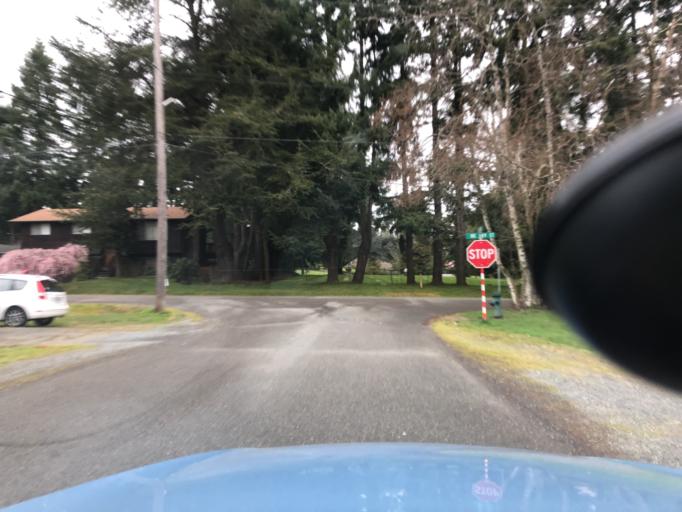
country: US
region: Washington
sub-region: King County
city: Lake Forest Park
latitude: 47.7365
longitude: -122.2938
